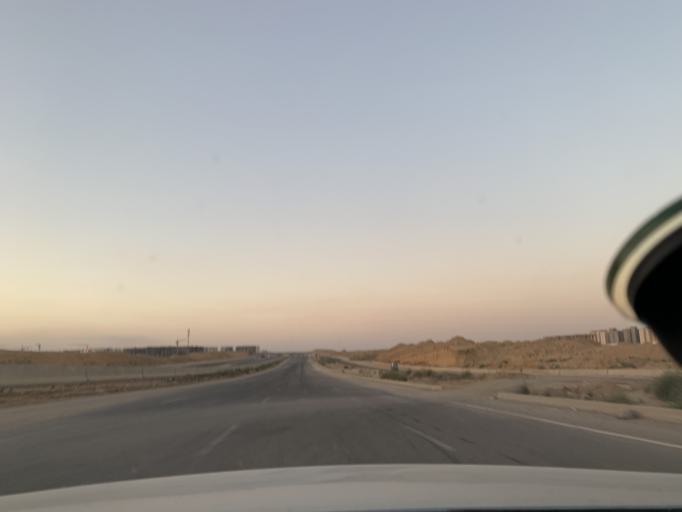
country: EG
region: Muhafazat al Qahirah
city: Halwan
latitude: 29.9578
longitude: 31.5436
